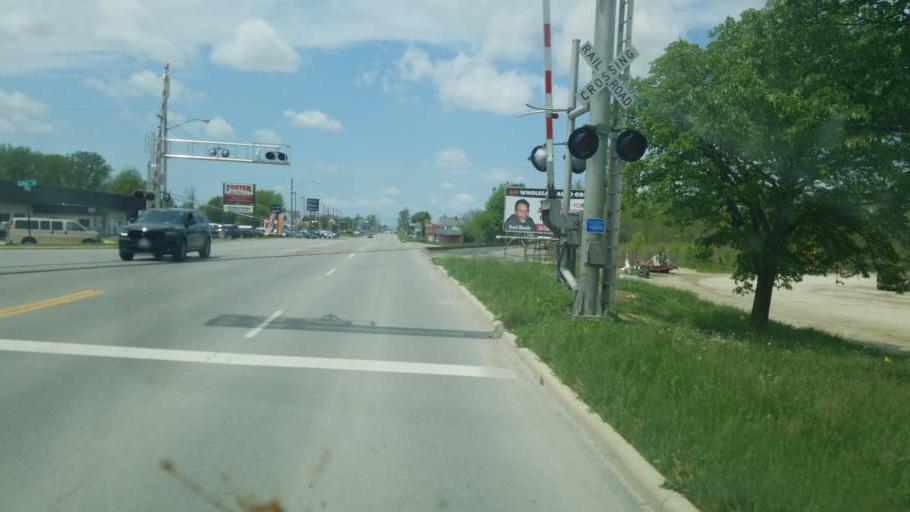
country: US
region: Ohio
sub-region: Sandusky County
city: Stony Prairie
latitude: 41.3578
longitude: -83.1386
